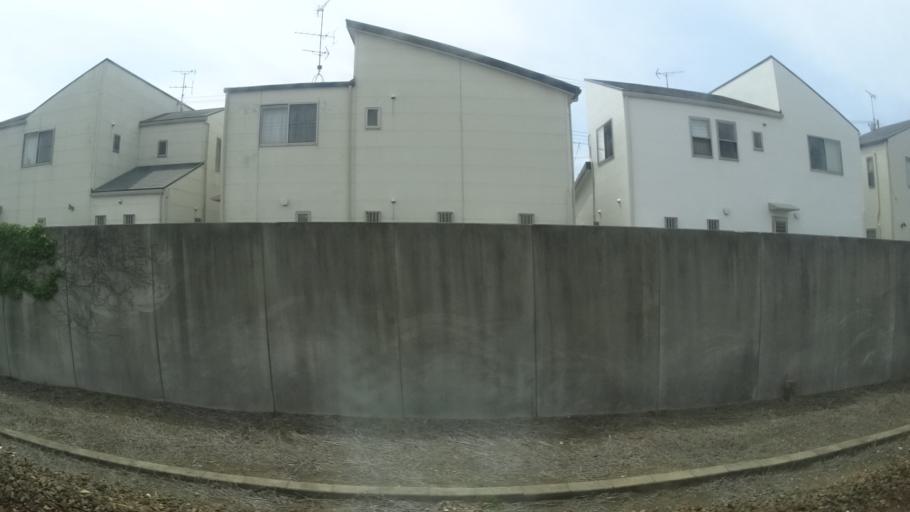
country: JP
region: Shizuoka
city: Hamamatsu
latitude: 34.6855
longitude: 137.6327
